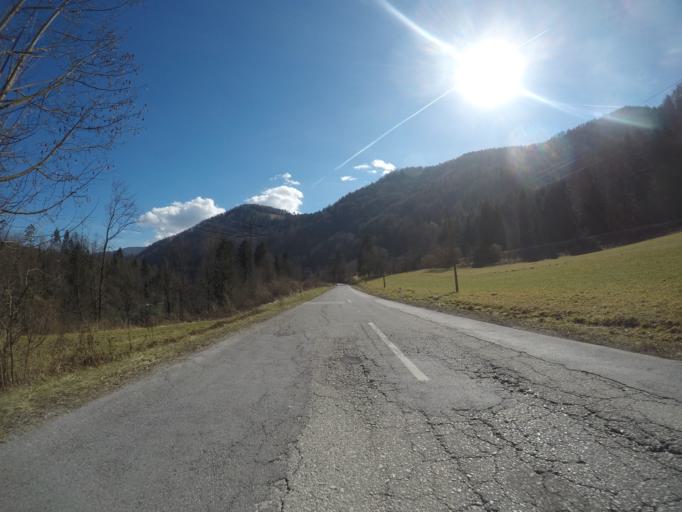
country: SI
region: Selnica ob Dravi
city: Selnica ob Dravi
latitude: 46.5364
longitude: 15.4546
